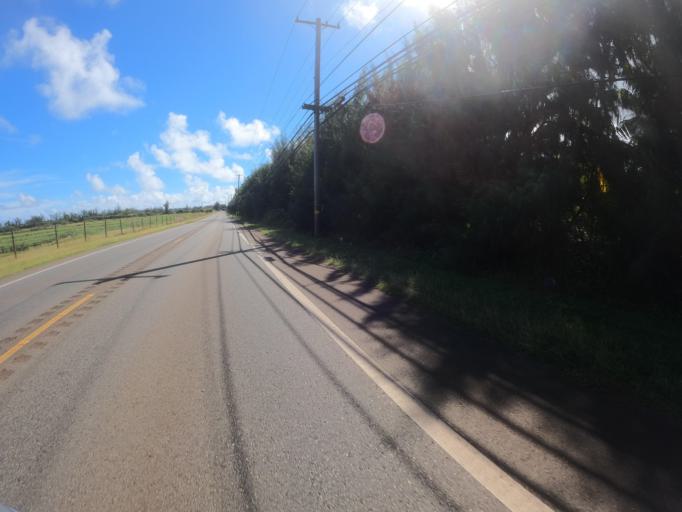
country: US
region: Hawaii
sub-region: Honolulu County
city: Kahuku
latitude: 21.6829
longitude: -157.9590
